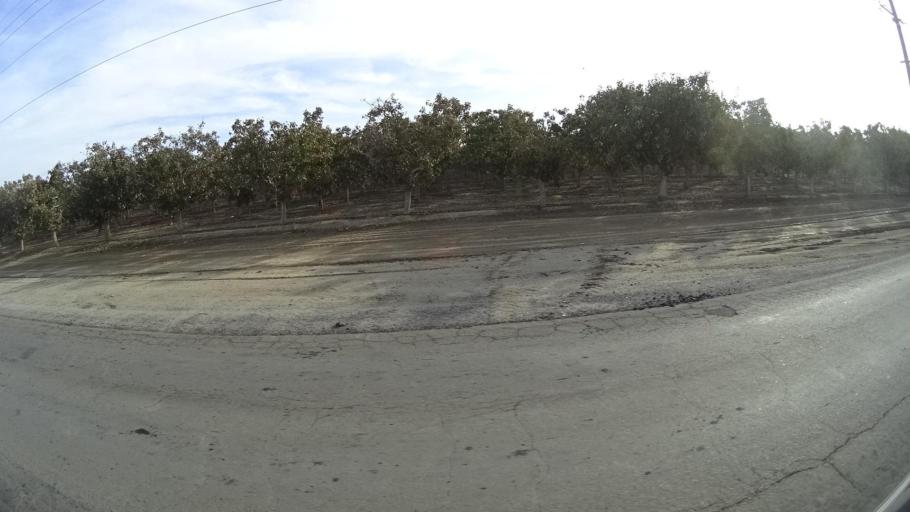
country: US
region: California
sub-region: Kern County
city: McFarland
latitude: 35.7291
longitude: -119.2052
